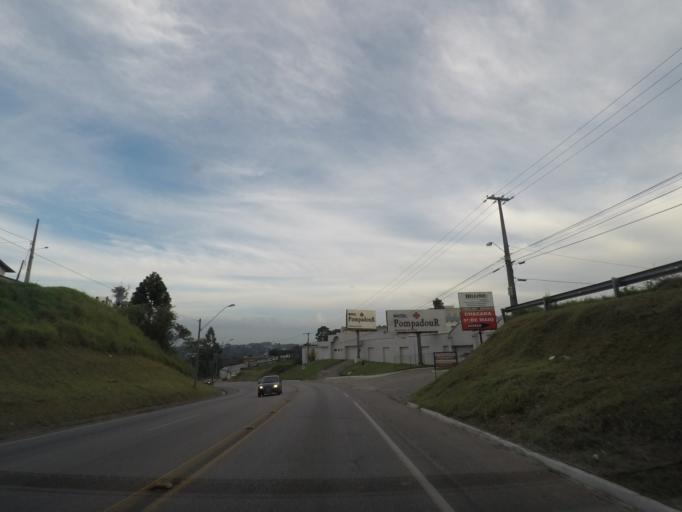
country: BR
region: Parana
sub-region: Colombo
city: Colombo
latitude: -25.3586
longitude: -49.2196
